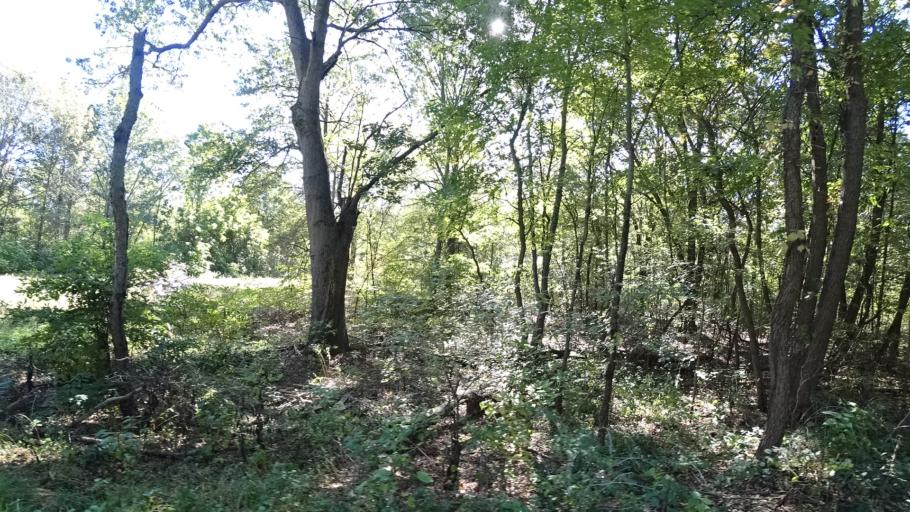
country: US
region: Indiana
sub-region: LaPorte County
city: Michigan City
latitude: 41.7004
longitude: -86.9124
